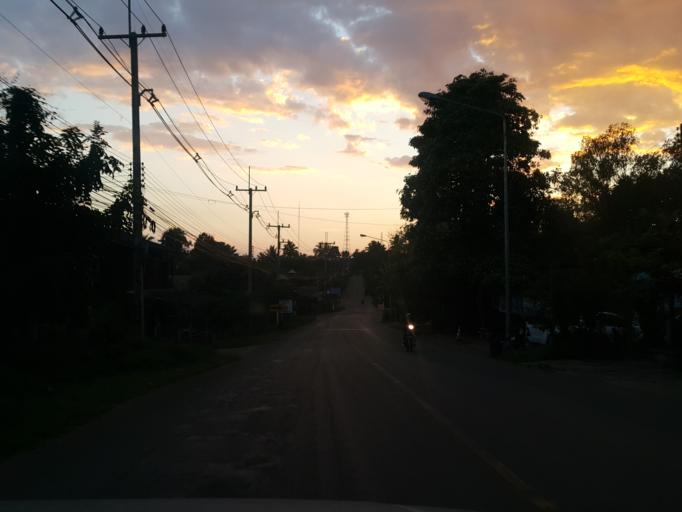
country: TH
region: Mae Hong Son
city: Khun Yuam
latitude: 18.8367
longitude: 97.9446
